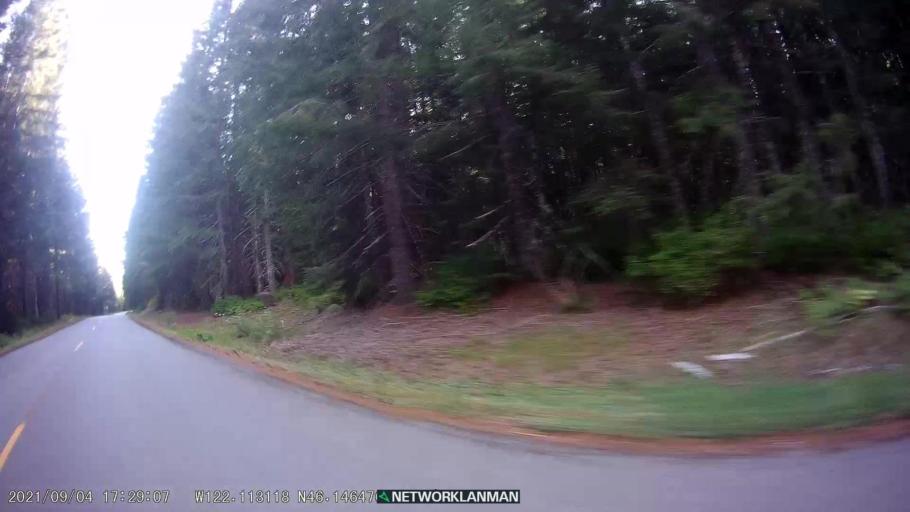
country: US
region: Washington
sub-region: Clark County
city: Yacolt
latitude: 46.1461
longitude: -122.1136
